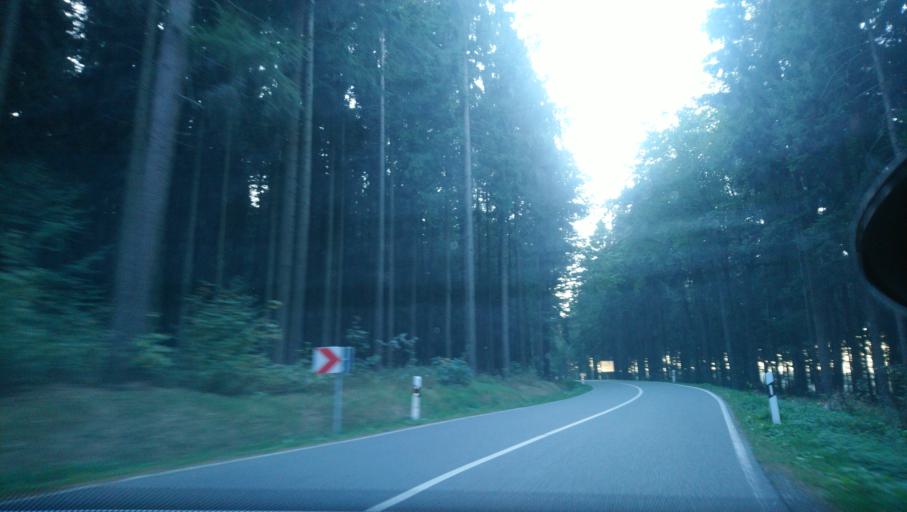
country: DE
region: Saxony
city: Thum
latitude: 50.6522
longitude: 12.9328
